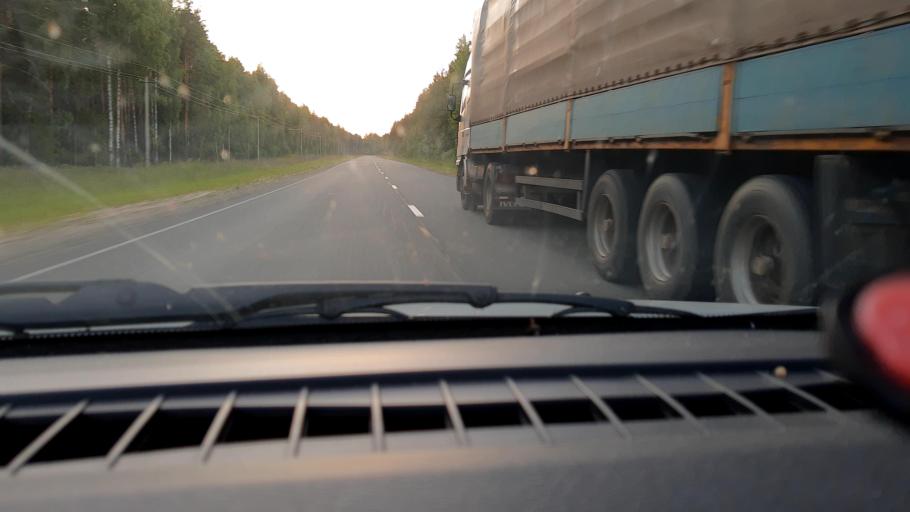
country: RU
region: Nizjnij Novgorod
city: Uren'
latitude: 57.3801
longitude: 45.6899
